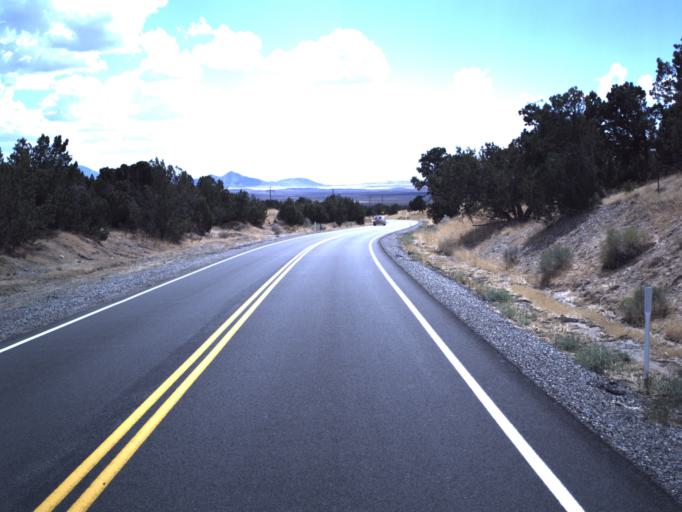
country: US
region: Utah
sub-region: Tooele County
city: Grantsville
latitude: 40.3241
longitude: -112.6248
